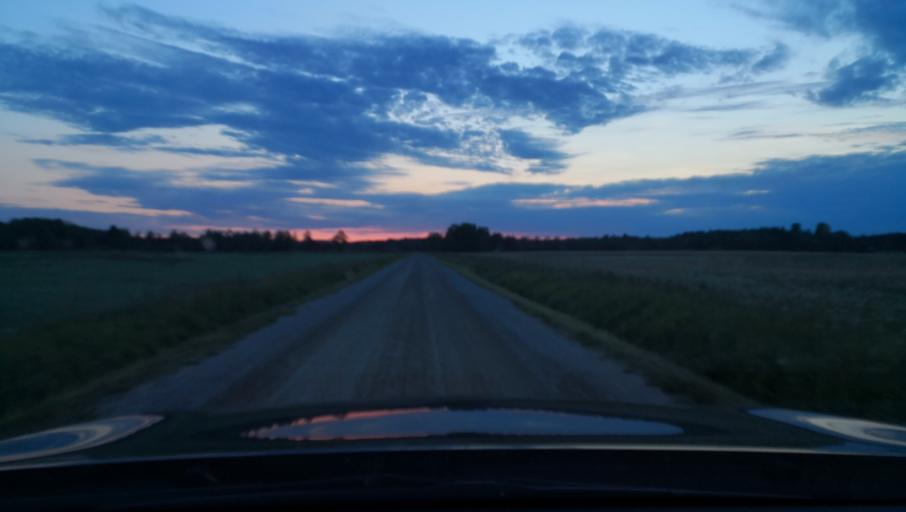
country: SE
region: Uppsala
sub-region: Heby Kommun
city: OEstervala
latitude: 60.0095
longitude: 17.3251
